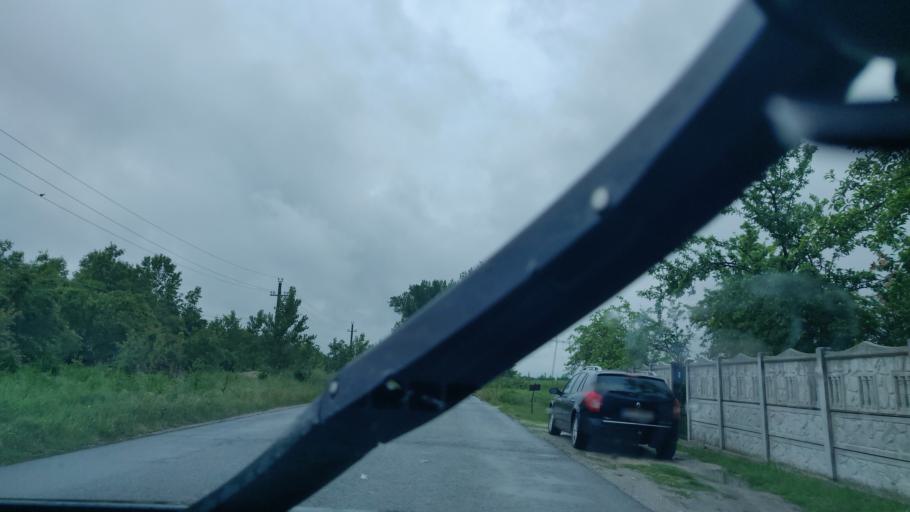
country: RO
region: Giurgiu
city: Iepuresti
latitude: 44.2685
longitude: 25.8482
